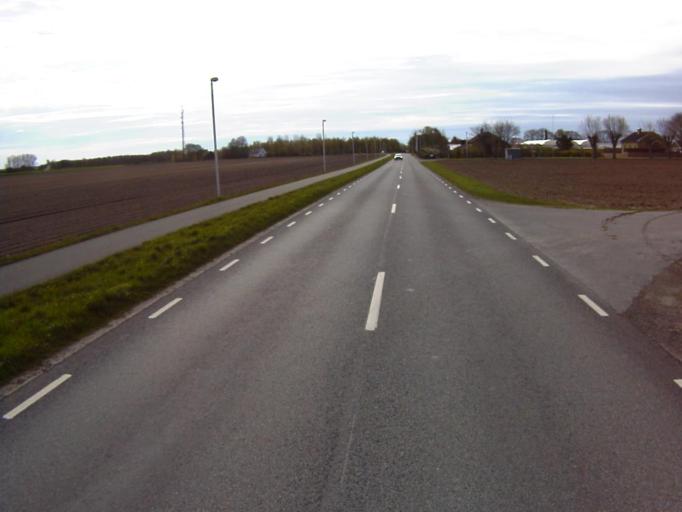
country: SE
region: Skane
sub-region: Kristianstads Kommun
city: Norra Asum
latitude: 56.0048
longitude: 14.1334
